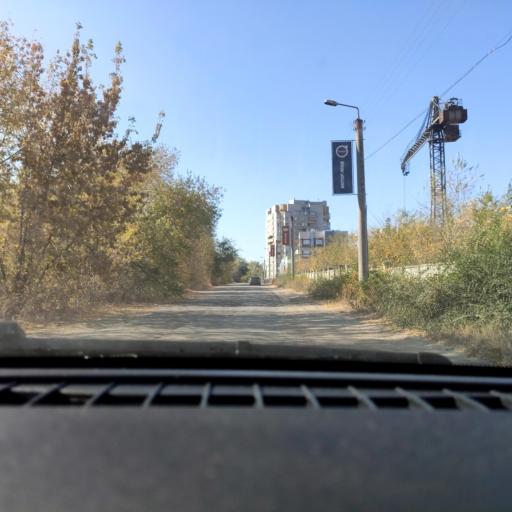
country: RU
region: Voronezj
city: Somovo
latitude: 51.6691
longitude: 39.2942
